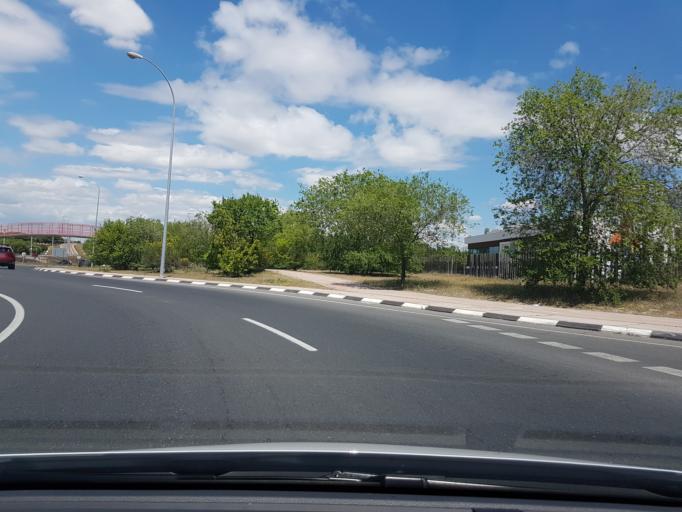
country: ES
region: Madrid
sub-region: Provincia de Madrid
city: Pozuelo de Alarcon
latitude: 40.4222
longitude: -3.8027
